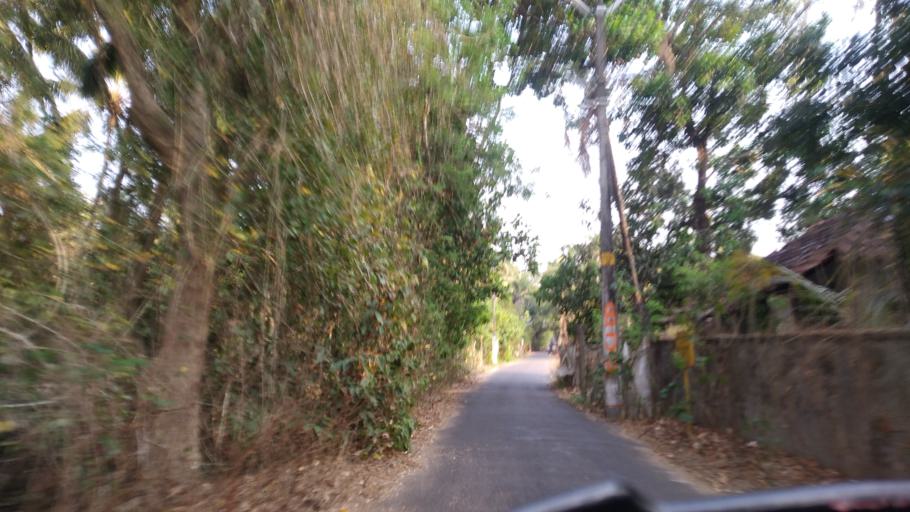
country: IN
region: Kerala
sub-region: Thrissur District
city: Thanniyam
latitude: 10.4275
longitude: 76.0809
